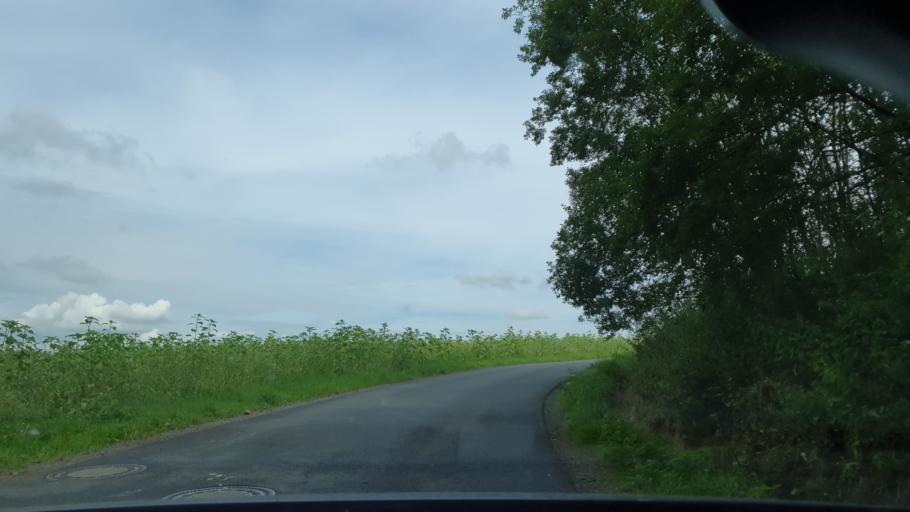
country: DE
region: North Rhine-Westphalia
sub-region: Regierungsbezirk Detmold
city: Werther
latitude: 52.0853
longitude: 8.4135
